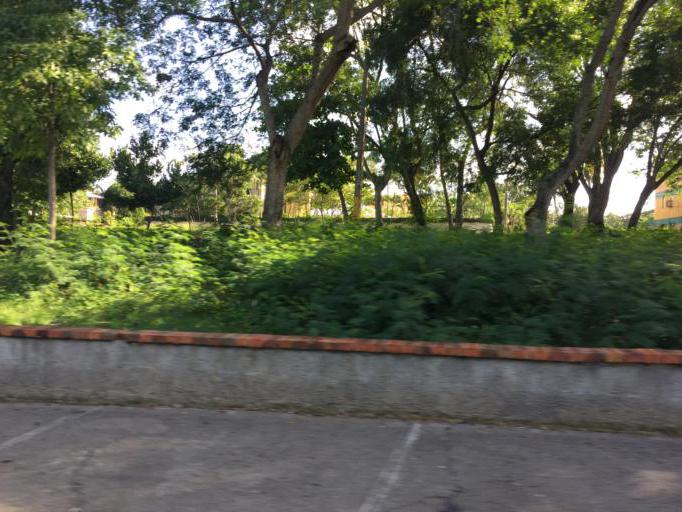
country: DO
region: Nacional
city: La Agustina
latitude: 18.4881
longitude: -69.9589
